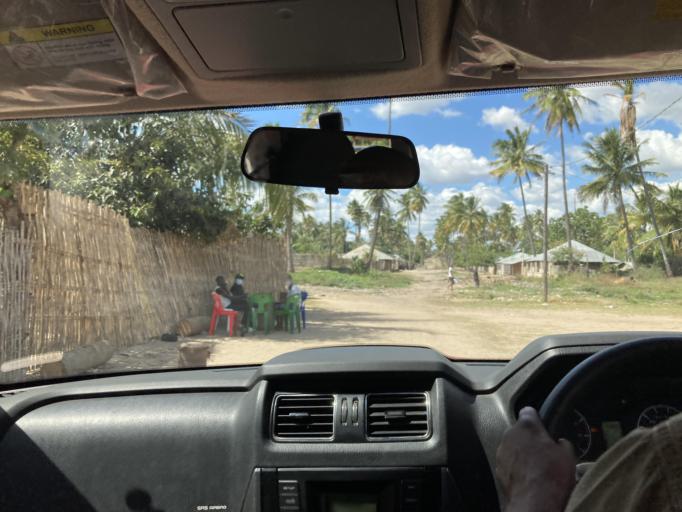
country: MZ
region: Cabo Delgado
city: Montepuez
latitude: -13.1305
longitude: 39.0076
